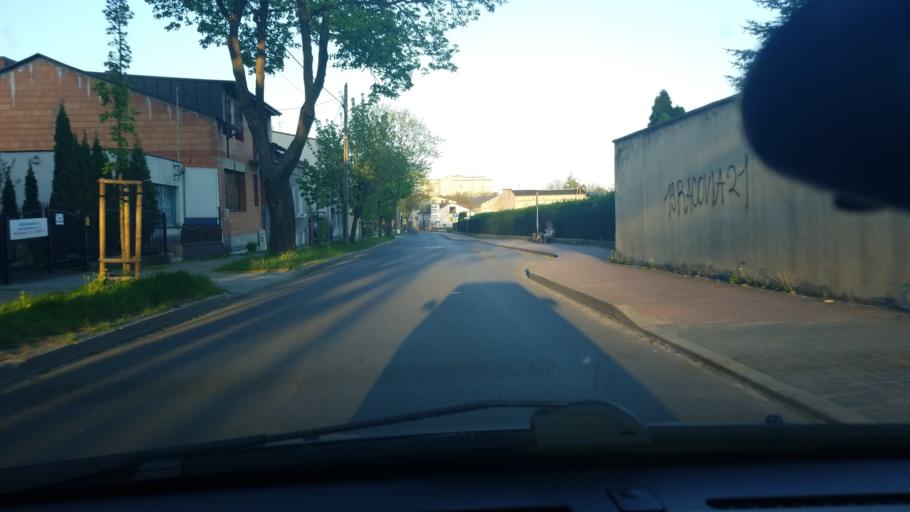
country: PL
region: Silesian Voivodeship
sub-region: Czestochowa
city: Czestochowa
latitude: 50.8048
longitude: 19.0953
